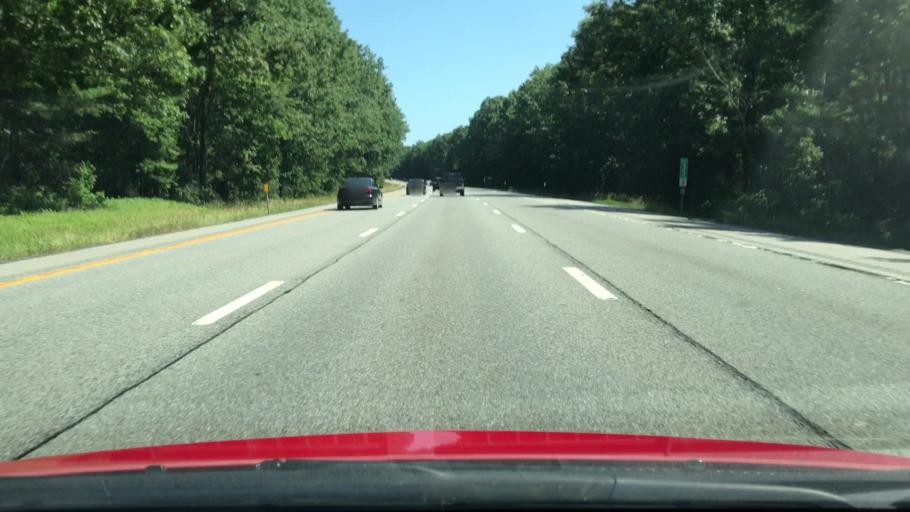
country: US
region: New York
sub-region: Saratoga County
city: Saratoga Springs
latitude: 43.1318
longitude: -73.7338
